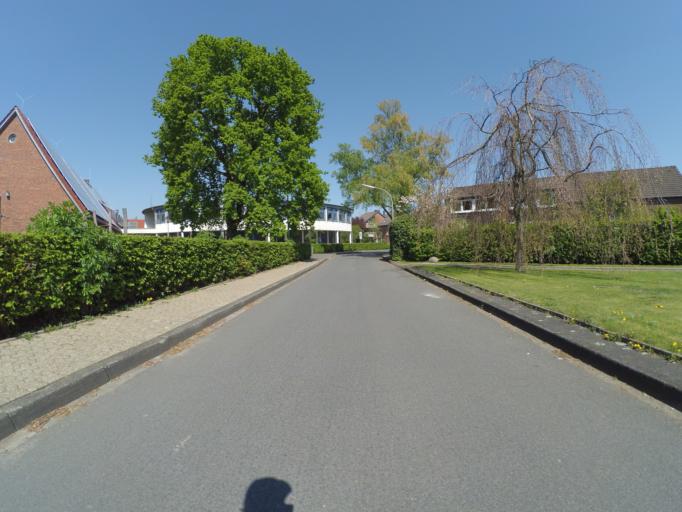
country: DE
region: North Rhine-Westphalia
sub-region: Regierungsbezirk Munster
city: Nordkirchen
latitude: 51.7406
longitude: 7.5277
